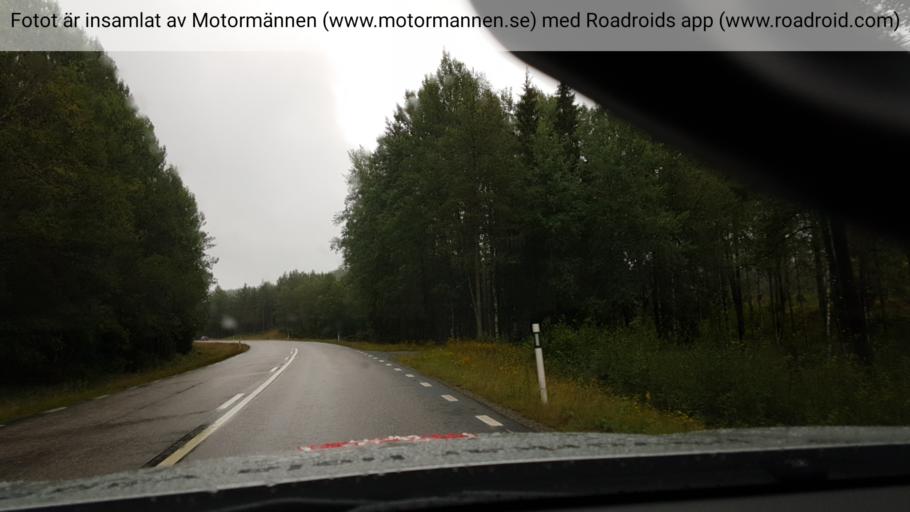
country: SE
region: Vaestra Goetaland
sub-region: Dals-Ed Kommun
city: Ed
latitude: 58.8758
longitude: 11.8327
